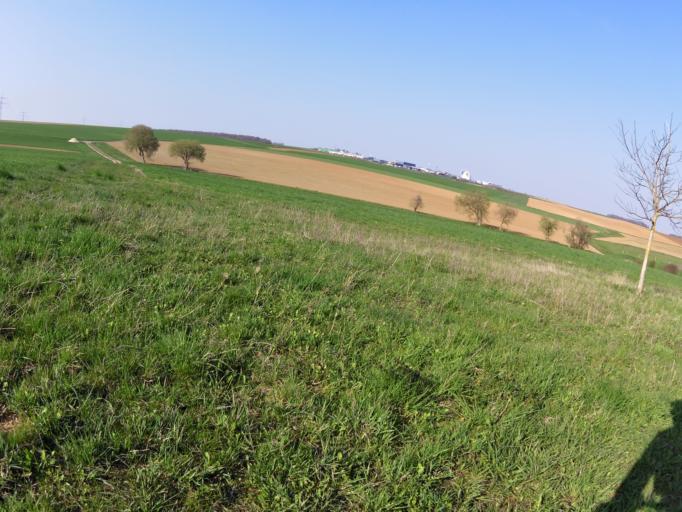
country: DE
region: Bavaria
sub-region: Regierungsbezirk Unterfranken
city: Theilheim
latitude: 49.7663
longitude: 10.0543
